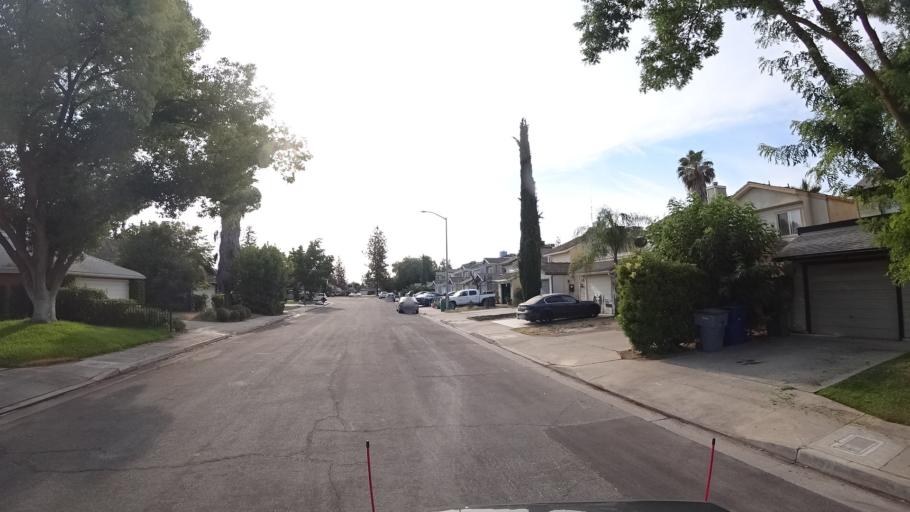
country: US
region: California
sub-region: Fresno County
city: West Park
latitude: 36.7730
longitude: -119.8595
